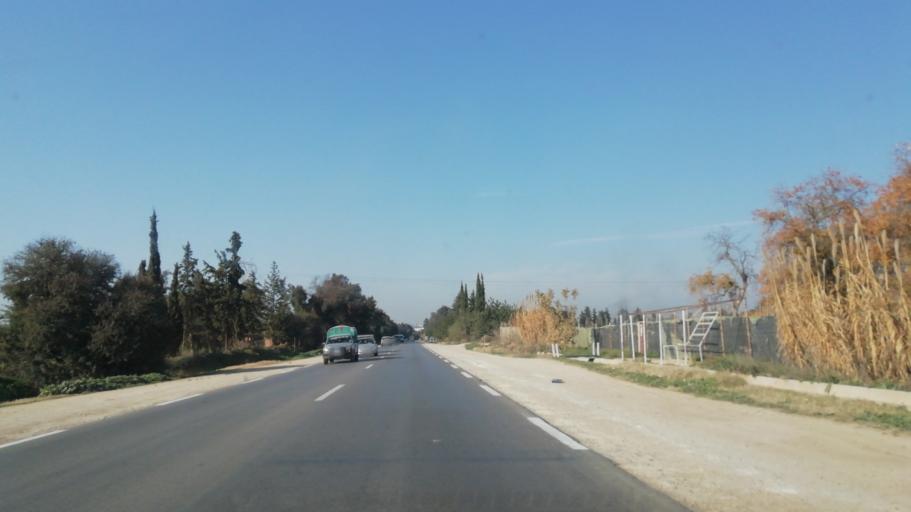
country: DZ
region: Relizane
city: Relizane
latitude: 35.7228
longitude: 0.4939
